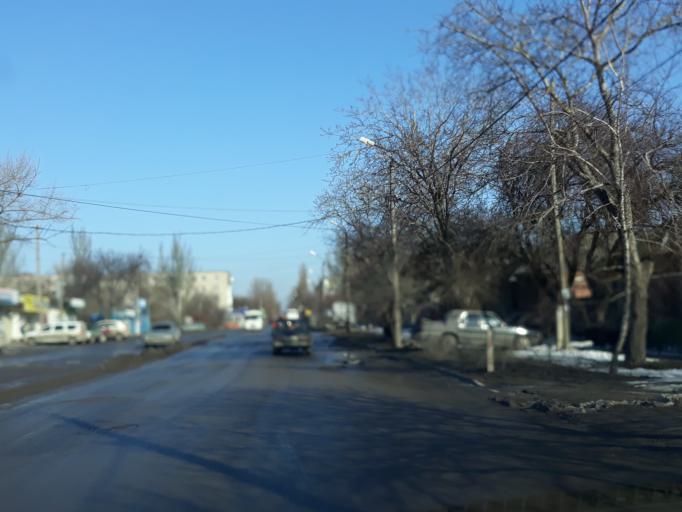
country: RU
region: Rostov
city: Taganrog
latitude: 47.2311
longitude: 38.8764
